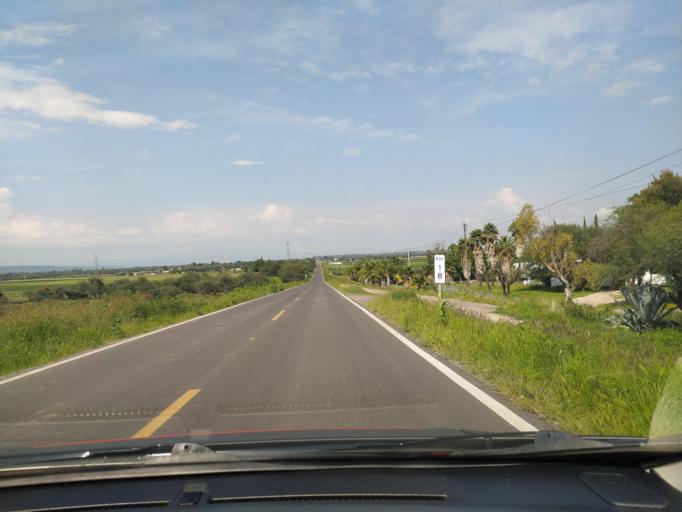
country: MX
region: Guanajuato
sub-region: San Francisco del Rincon
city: Fraccionamiento la Mezquitera
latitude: 20.9908
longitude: -101.8251
